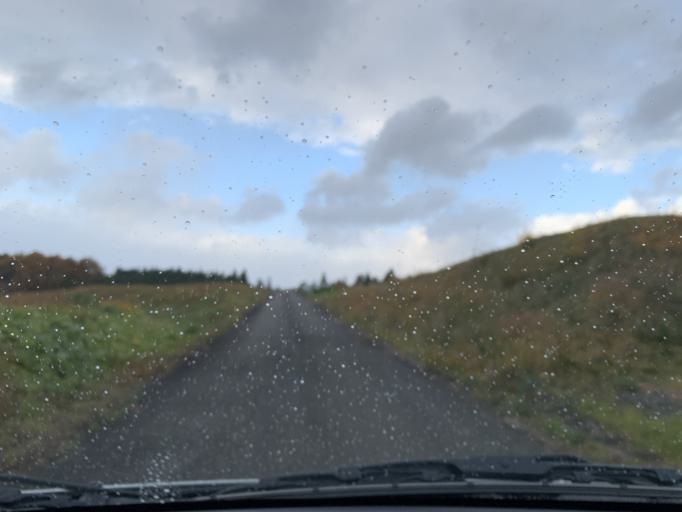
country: JP
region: Iwate
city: Mizusawa
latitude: 39.0868
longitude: 141.0049
